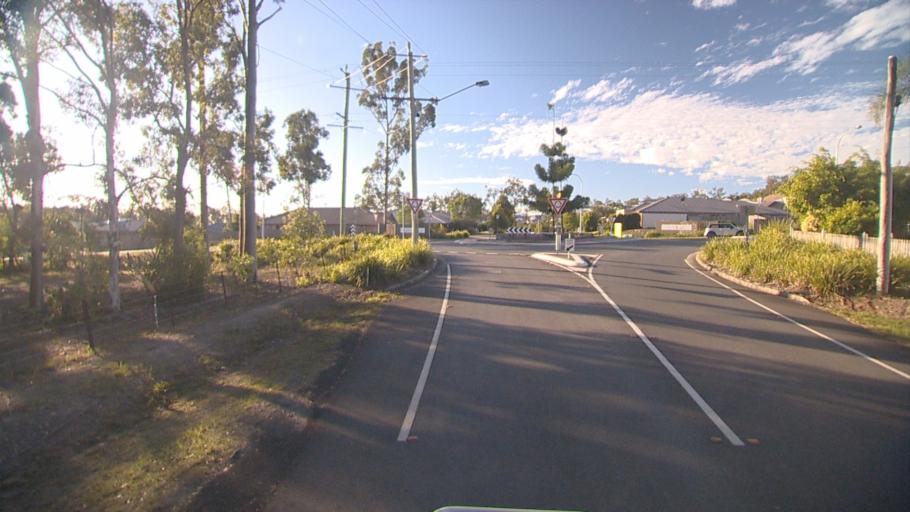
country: AU
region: Queensland
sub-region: Logan
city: Waterford West
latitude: -27.7202
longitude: 153.1541
